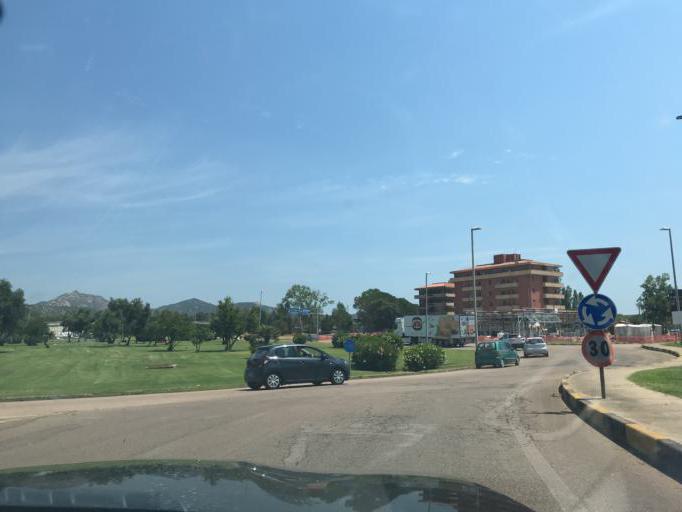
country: IT
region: Sardinia
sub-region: Provincia di Olbia-Tempio
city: Olbia
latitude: 40.9307
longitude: 9.5090
